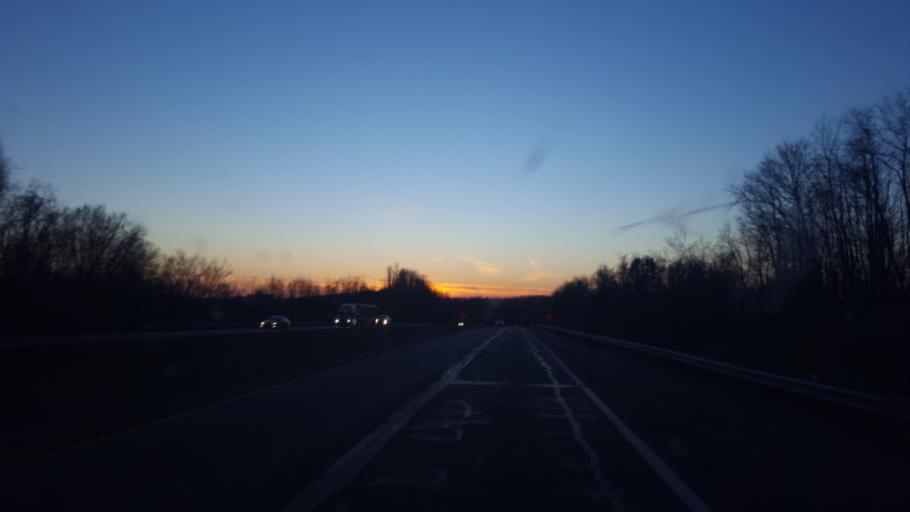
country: US
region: Ohio
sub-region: Belmont County
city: Bethesda
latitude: 40.0594
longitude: -81.0906
